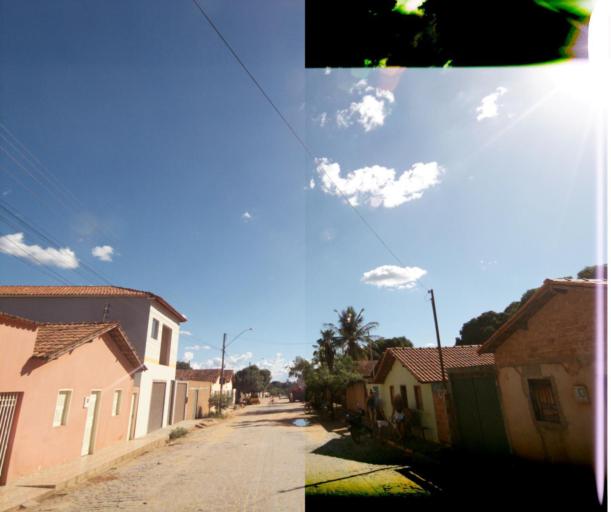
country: BR
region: Bahia
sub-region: Carinhanha
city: Carinhanha
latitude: -14.1834
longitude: -44.5418
